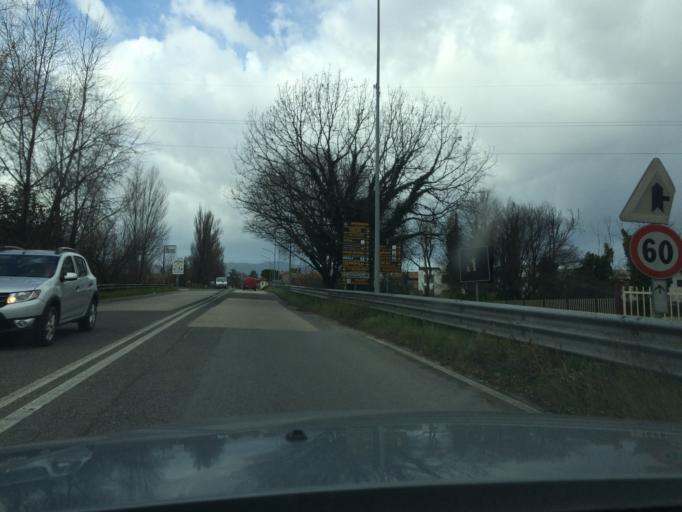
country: IT
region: Umbria
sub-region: Provincia di Terni
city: Terni
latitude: 42.5455
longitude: 12.6035
